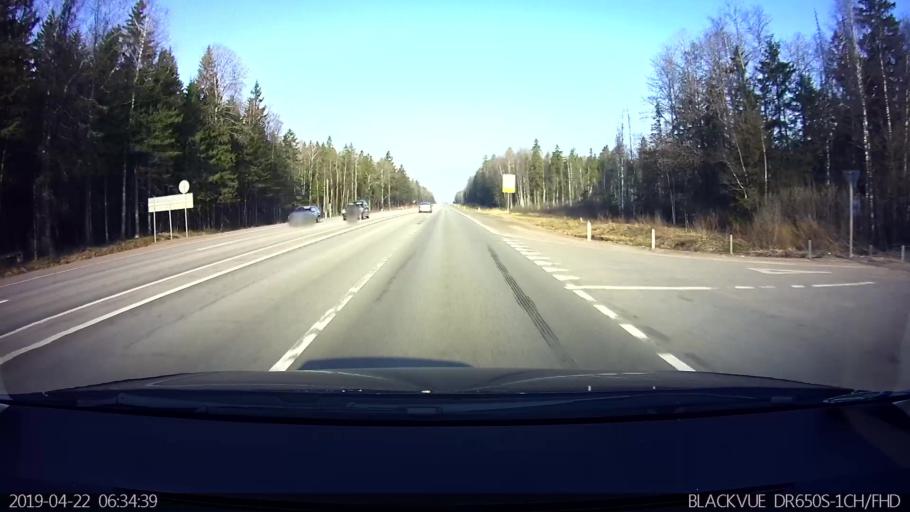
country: RU
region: Moskovskaya
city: Uvarovka
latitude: 55.4743
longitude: 35.4917
